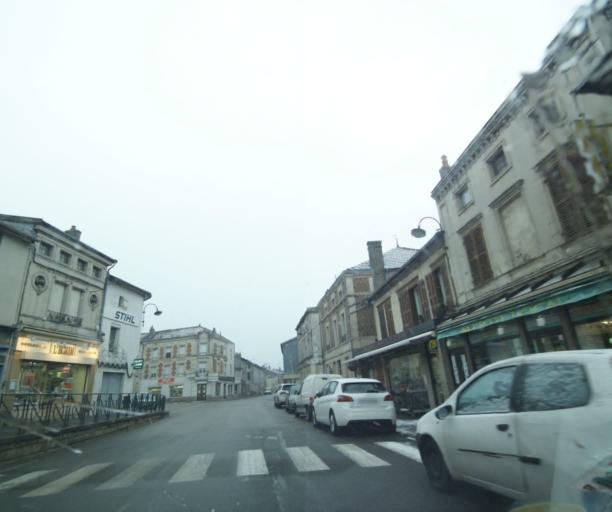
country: FR
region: Champagne-Ardenne
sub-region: Departement de la Haute-Marne
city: Wassy
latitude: 48.4977
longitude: 4.9486
